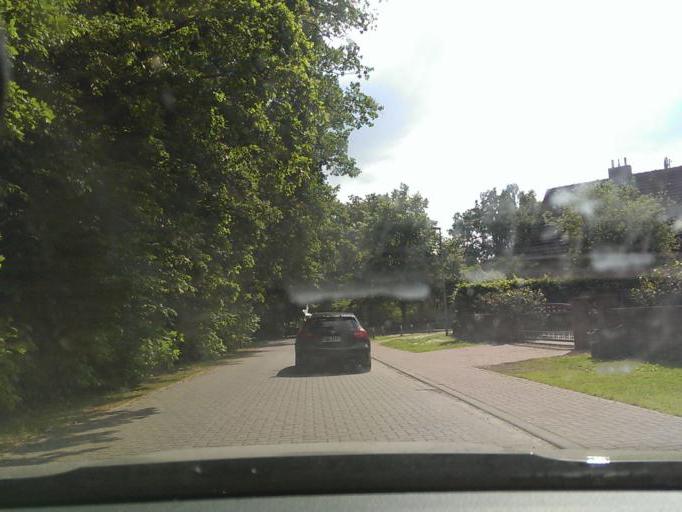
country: DE
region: Lower Saxony
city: Lindwedel
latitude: 52.5503
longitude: 9.6767
